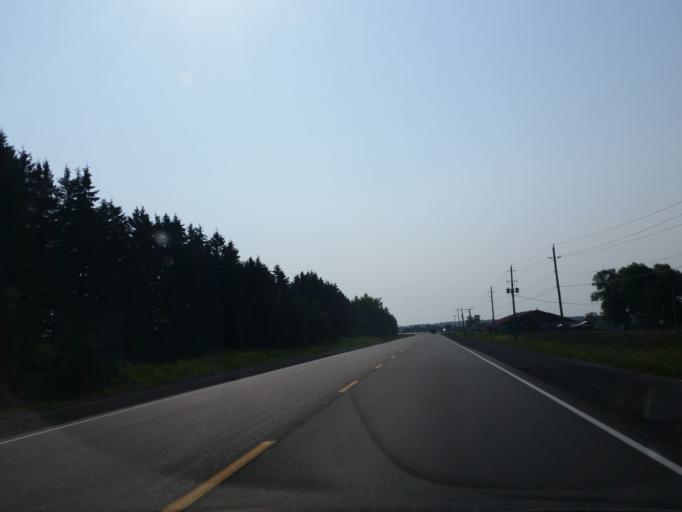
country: CA
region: Ontario
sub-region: Nipissing District
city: North Bay
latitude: 46.4085
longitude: -80.1041
